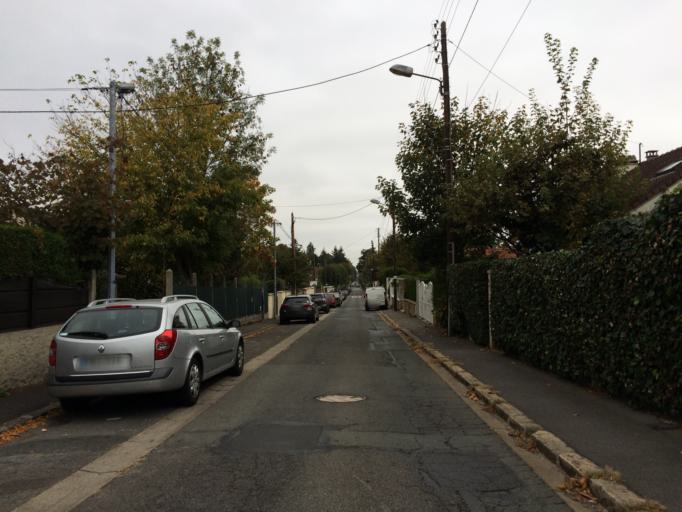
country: FR
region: Ile-de-France
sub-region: Departement de l'Essonne
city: Orsay
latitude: 48.6990
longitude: 2.2028
